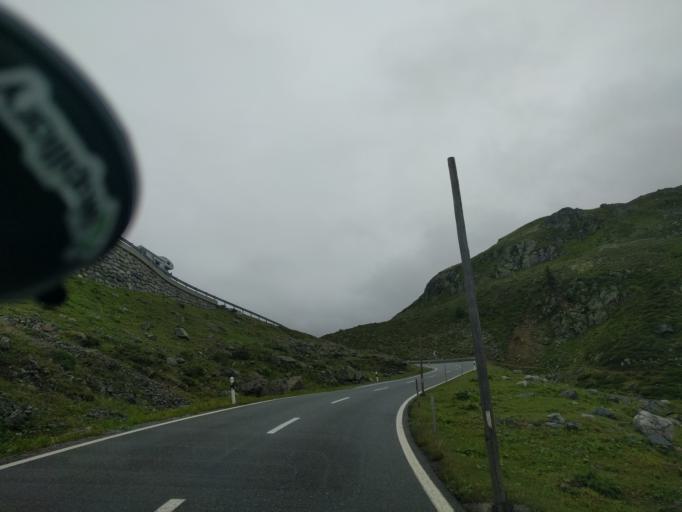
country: CH
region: Grisons
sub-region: Praettigau/Davos District
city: Davos
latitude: 46.7728
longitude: 9.9361
